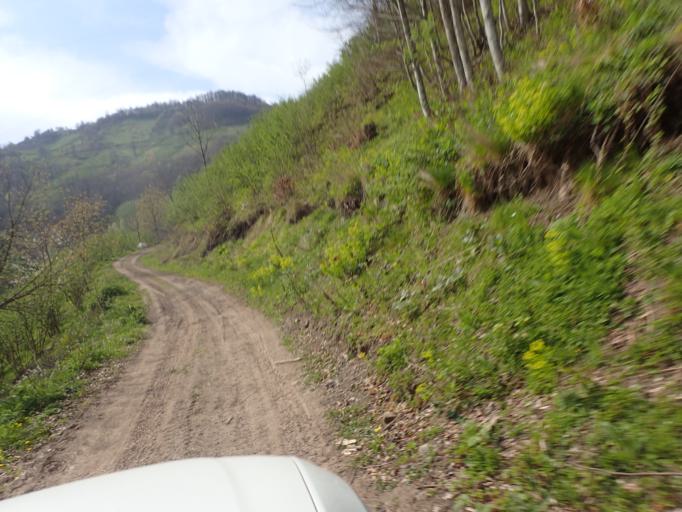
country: TR
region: Ordu
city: Aybasti
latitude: 40.7205
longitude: 37.2993
